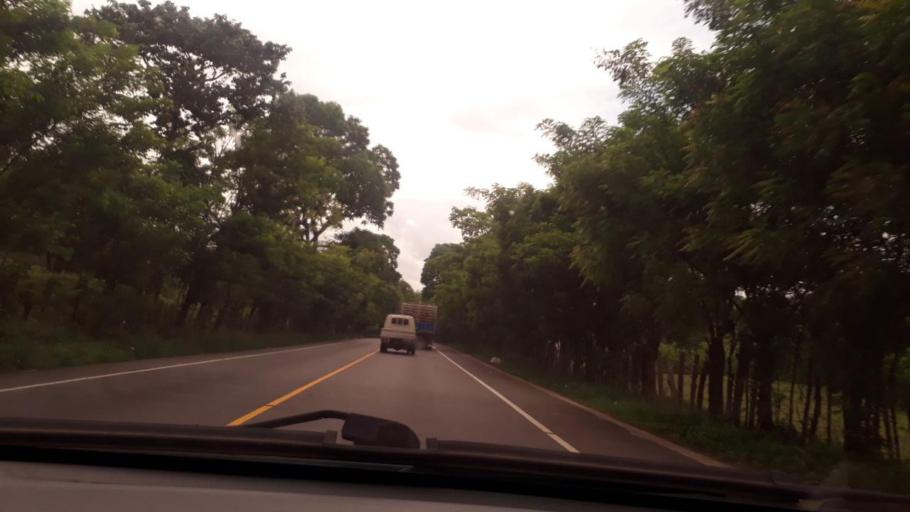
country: GT
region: Izabal
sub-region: Municipio de Los Amates
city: Los Amates
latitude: 15.2459
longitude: -89.1630
